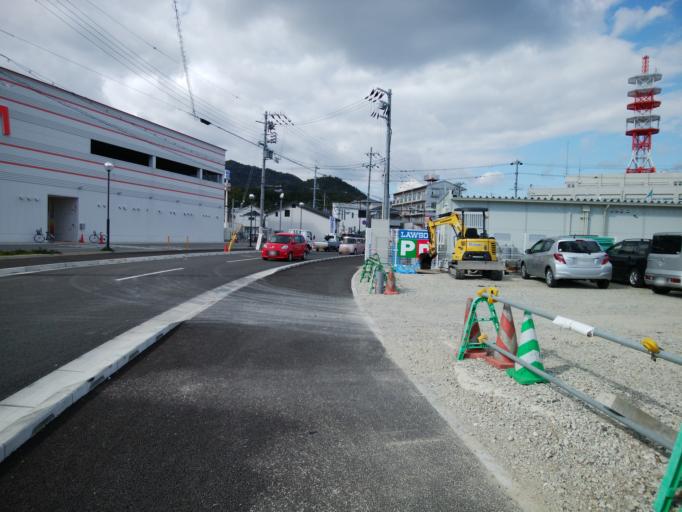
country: JP
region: Osaka
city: Ikeda
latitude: 34.8378
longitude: 135.4190
